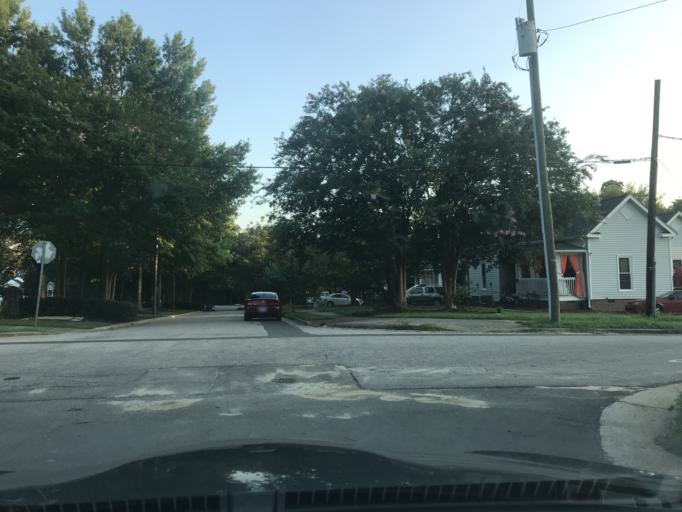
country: US
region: North Carolina
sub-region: Wake County
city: Raleigh
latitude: 35.7742
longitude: -78.6315
